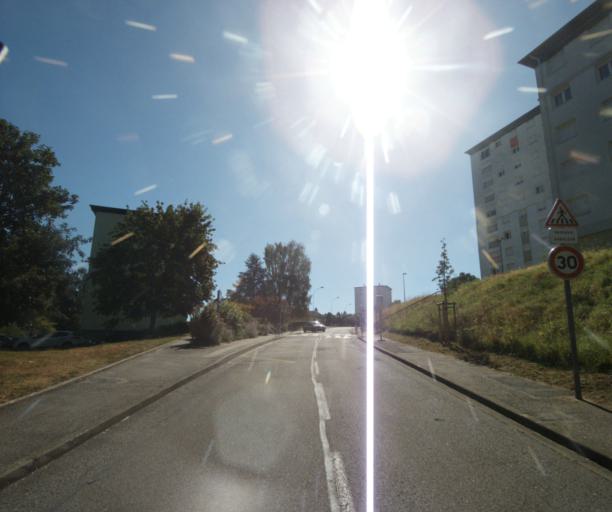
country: FR
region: Lorraine
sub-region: Departement des Vosges
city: Epinal
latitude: 48.1886
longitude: 6.4581
